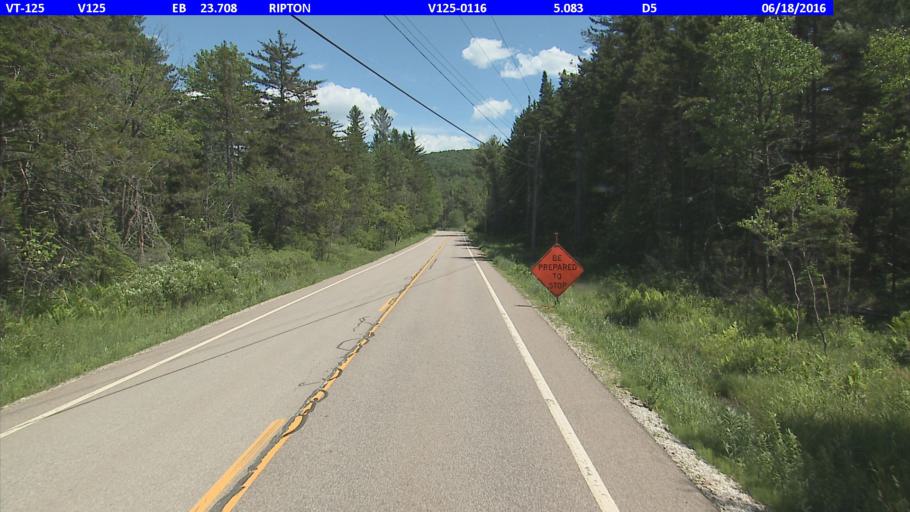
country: US
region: Vermont
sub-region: Rutland County
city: Brandon
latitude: 43.9463
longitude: -72.9794
